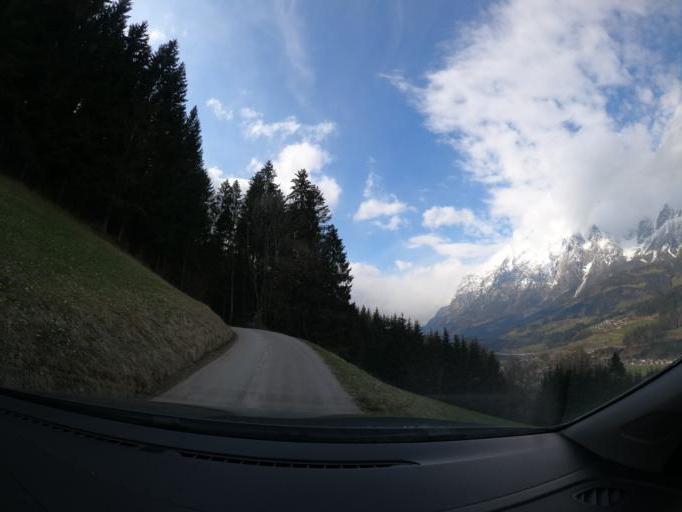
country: AT
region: Salzburg
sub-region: Politischer Bezirk Sankt Johann im Pongau
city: Pfarrwerfen
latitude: 47.4497
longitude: 13.1972
